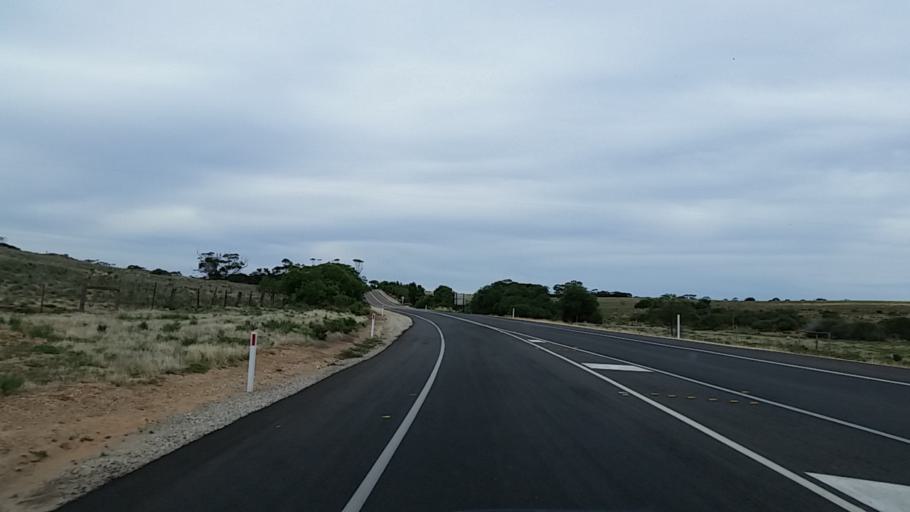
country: AU
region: South Australia
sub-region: Mid Murray
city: Mannum
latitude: -34.9324
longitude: 139.2404
